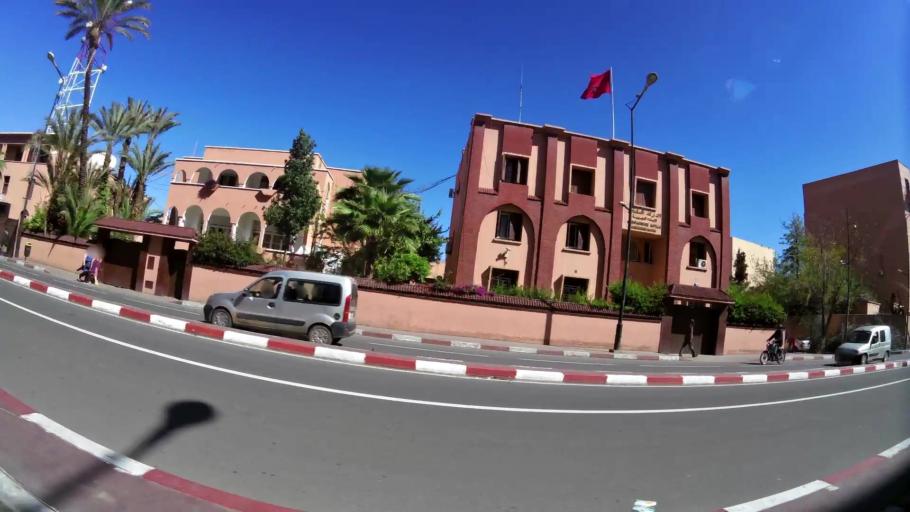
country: MA
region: Marrakech-Tensift-Al Haouz
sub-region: Marrakech
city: Marrakesh
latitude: 31.6330
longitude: -8.0048
